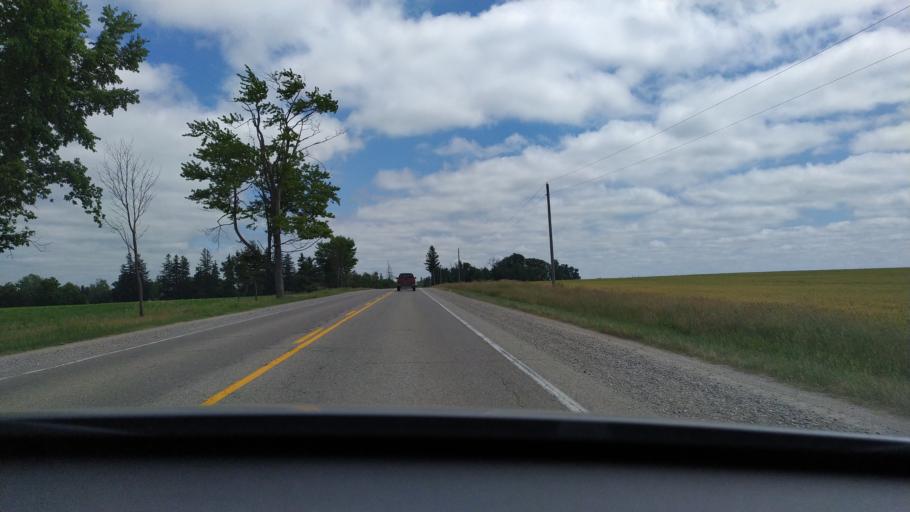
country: CA
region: Ontario
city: Stratford
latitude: 43.3065
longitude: -80.9791
